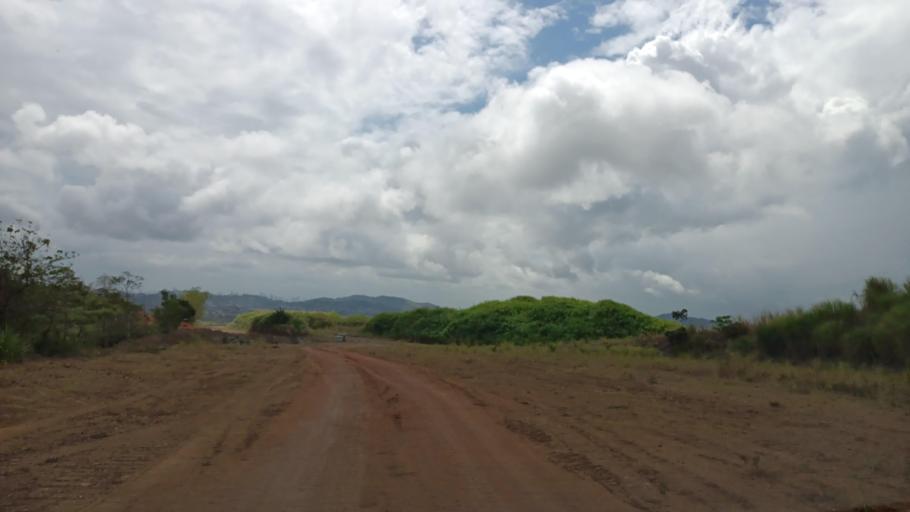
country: PA
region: Panama
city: La Cabima
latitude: 9.1144
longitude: -79.4980
